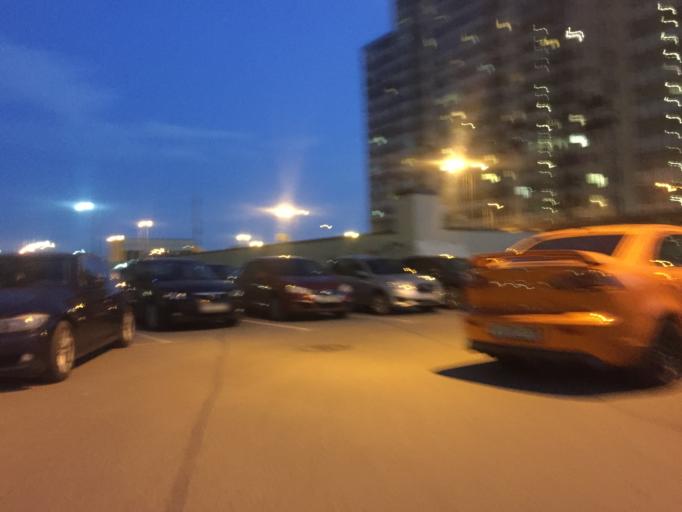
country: RU
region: Leningrad
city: Murino
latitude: 60.0493
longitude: 30.4314
